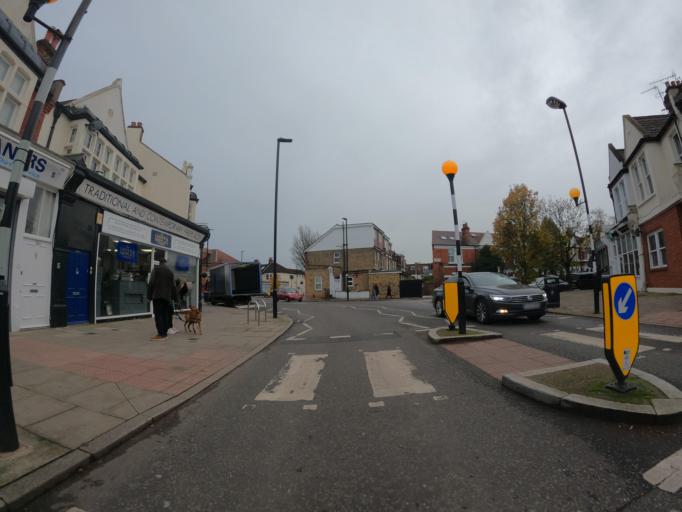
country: GB
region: England
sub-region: Greater London
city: Acton
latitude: 51.5013
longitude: -0.2571
